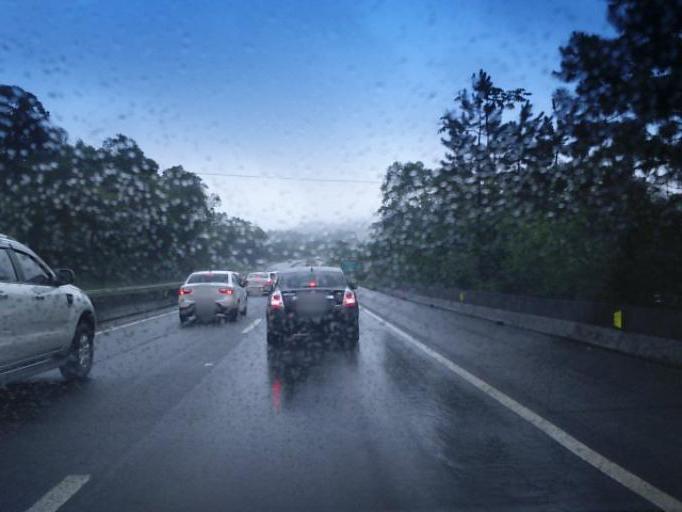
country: BR
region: Santa Catarina
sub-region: Joinville
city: Joinville
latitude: -26.1524
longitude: -48.9086
